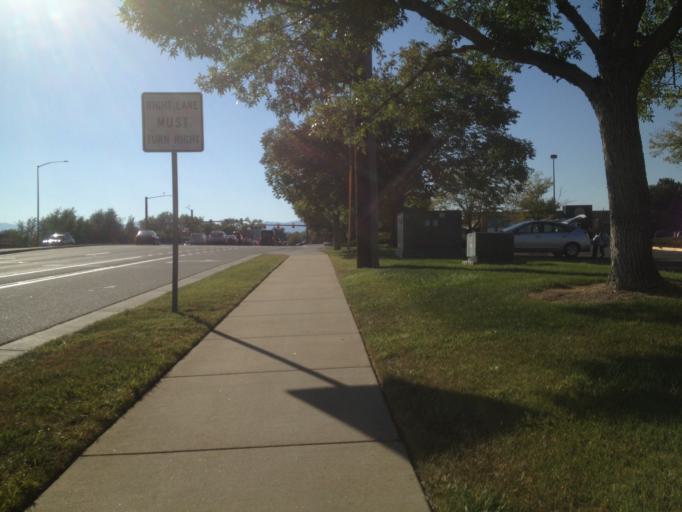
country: US
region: Colorado
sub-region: Boulder County
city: Louisville
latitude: 39.9870
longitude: -105.1260
